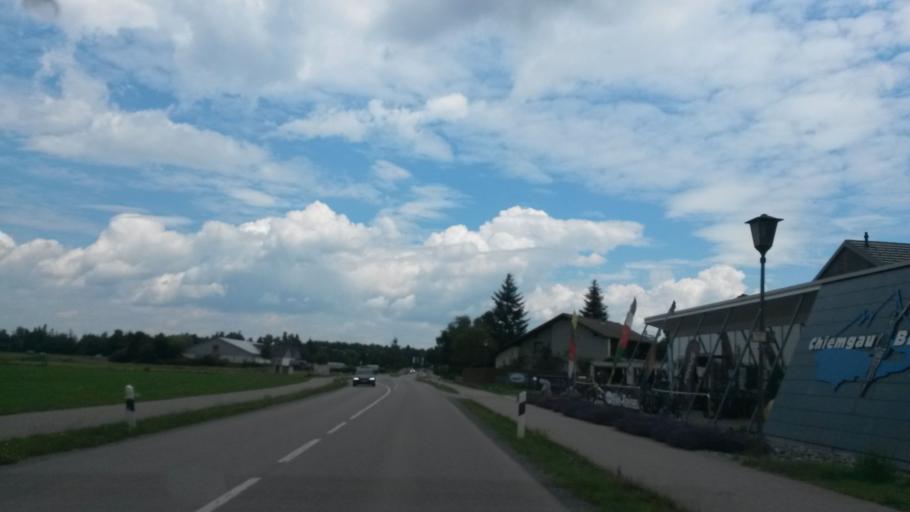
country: DE
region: Bavaria
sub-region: Upper Bavaria
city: Bernau am Chiemsee
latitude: 47.8224
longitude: 12.3829
